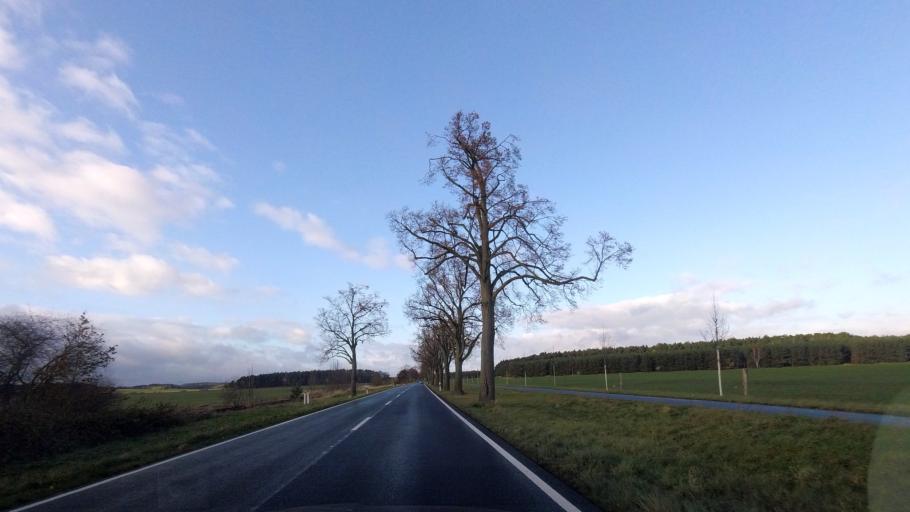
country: DE
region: Brandenburg
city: Belzig
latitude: 52.1162
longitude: 12.6445
